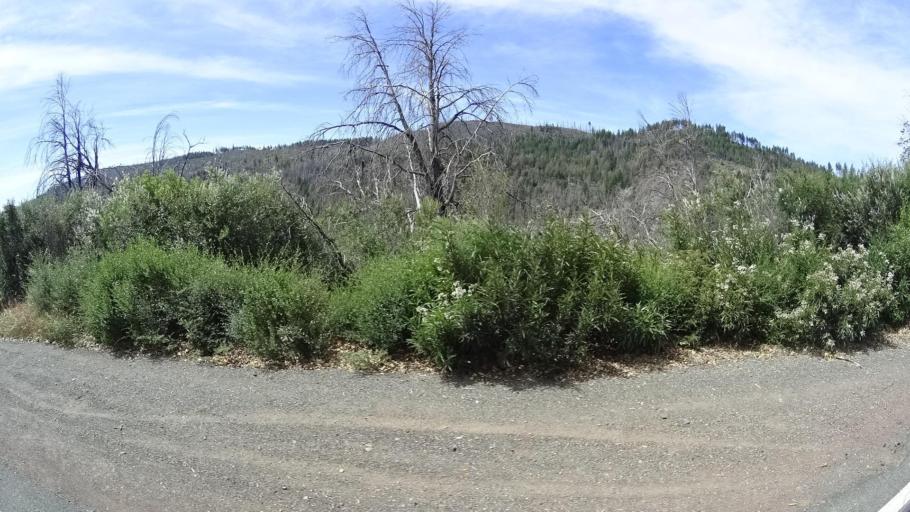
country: US
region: California
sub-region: Lake County
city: Cobb
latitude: 38.8546
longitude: -122.7033
